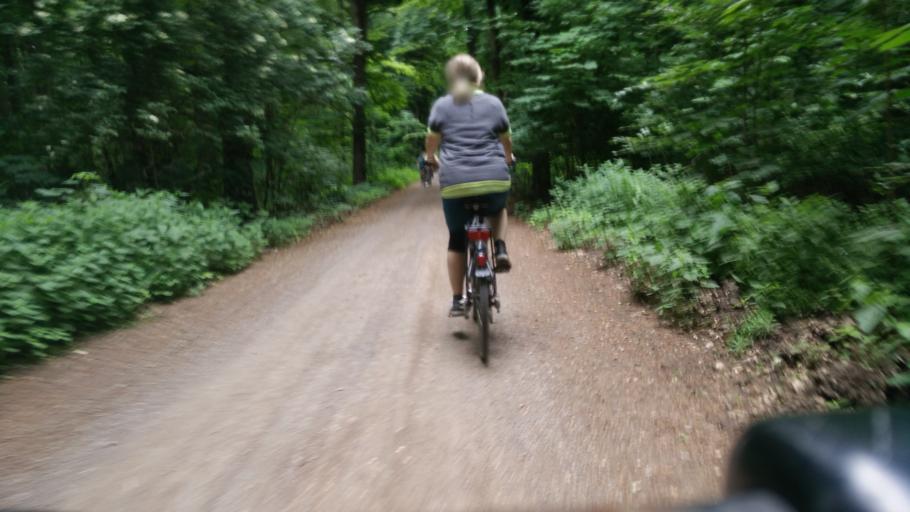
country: DE
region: Lower Saxony
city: Wunstorf
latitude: 52.4384
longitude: 9.3932
